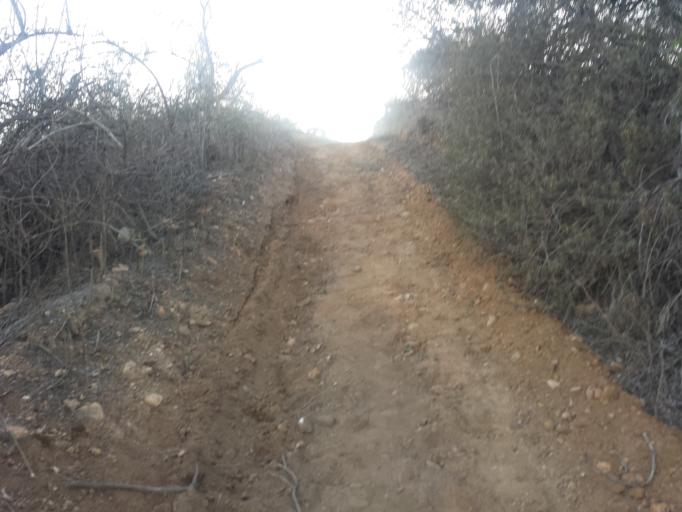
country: US
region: California
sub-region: Los Angeles County
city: Avocado Heights
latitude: 34.0055
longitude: -118.0040
